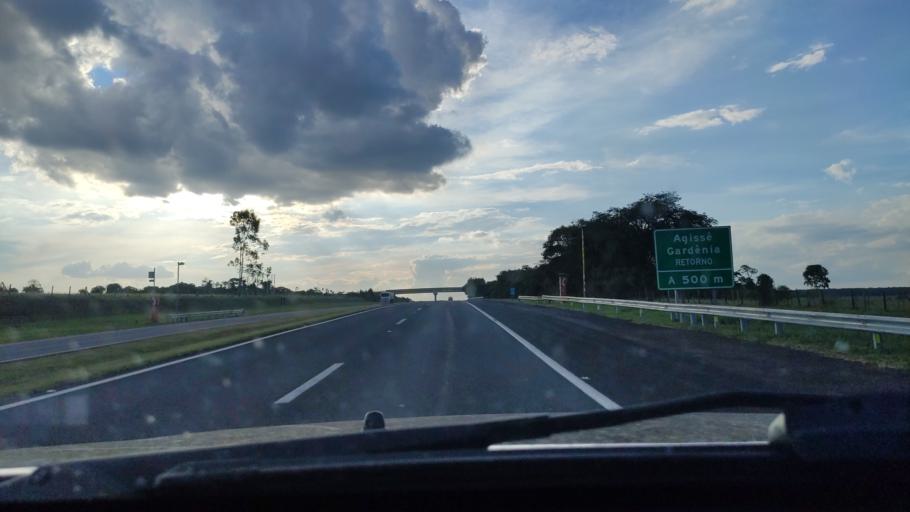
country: BR
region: Sao Paulo
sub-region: Rancharia
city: Rancharia
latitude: -22.4845
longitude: -50.9235
